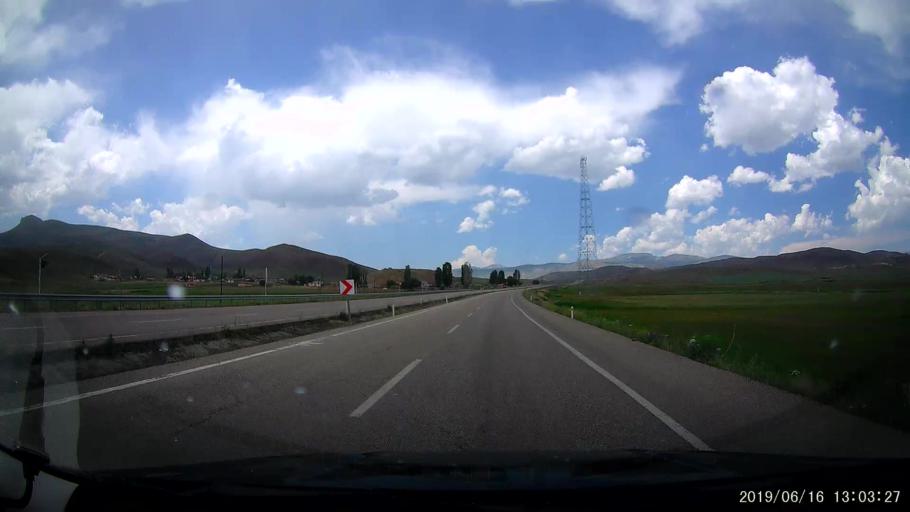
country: TR
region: Agri
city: Sulucem
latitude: 39.5815
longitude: 43.7901
